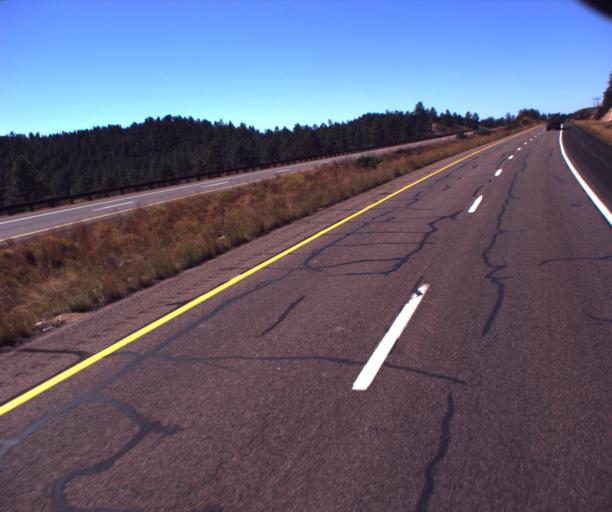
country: US
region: Arizona
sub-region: Gila County
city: Star Valley
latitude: 34.2801
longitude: -111.1518
